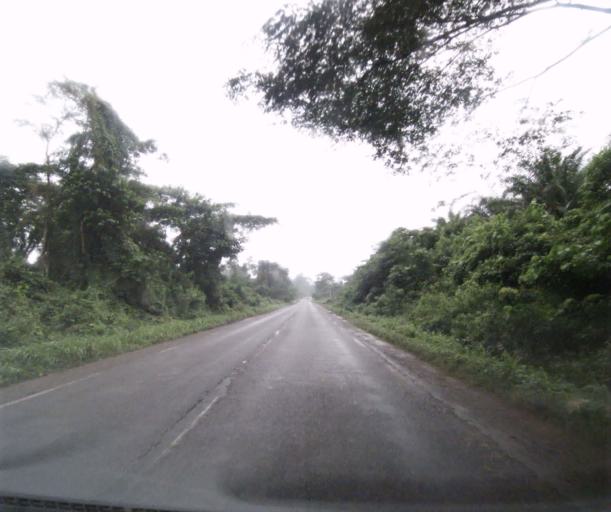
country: CM
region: Centre
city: Eseka
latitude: 3.8901
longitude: 10.7574
